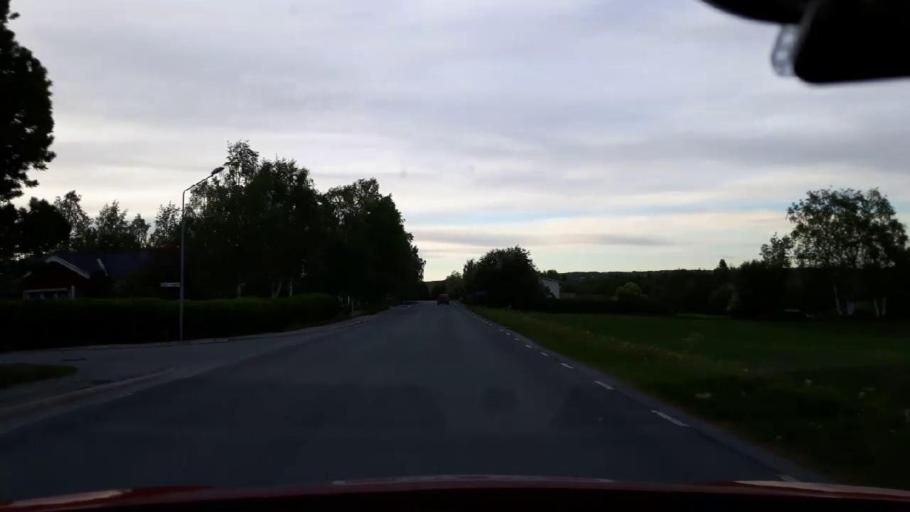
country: SE
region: Jaemtland
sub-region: OEstersunds Kommun
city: Ostersund
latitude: 62.9882
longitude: 14.5793
